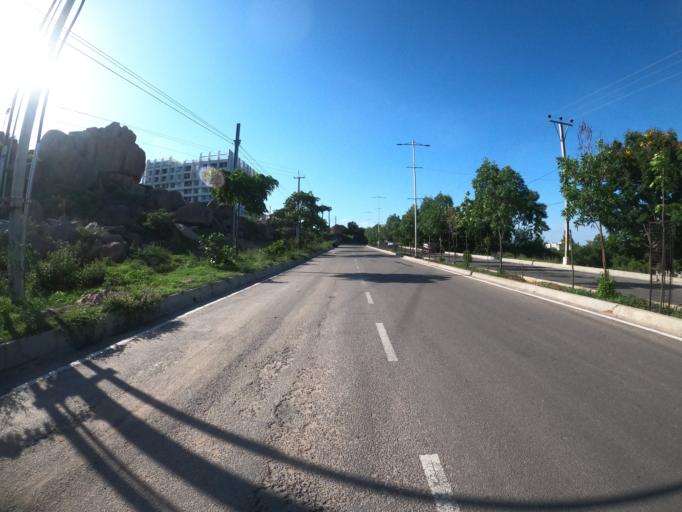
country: IN
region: Telangana
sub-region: Hyderabad
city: Hyderabad
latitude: 17.3531
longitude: 78.3697
